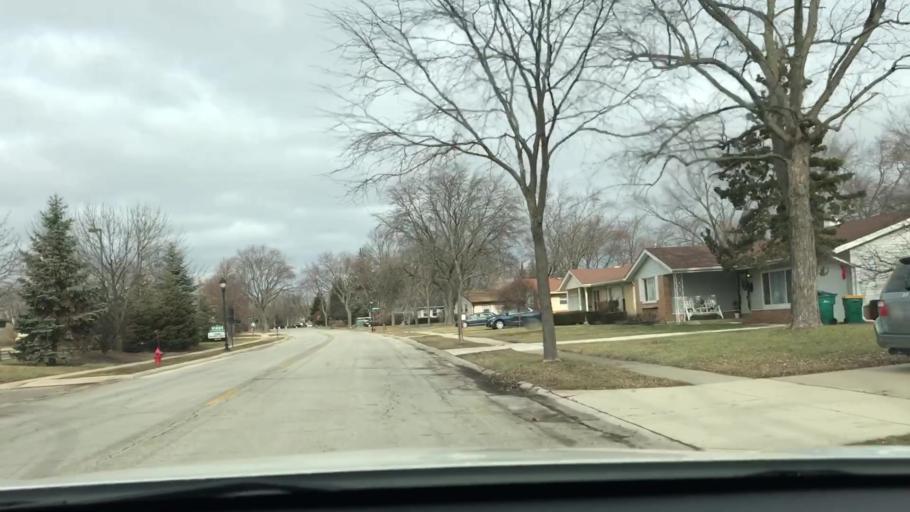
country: US
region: Illinois
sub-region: Cook County
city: Elk Grove Village
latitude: 42.0091
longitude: -87.9895
